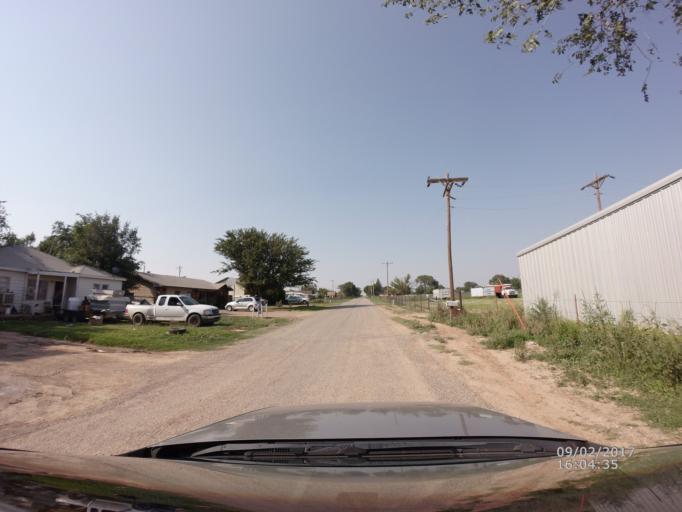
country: US
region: New Mexico
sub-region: Curry County
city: Clovis
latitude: 34.4442
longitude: -103.1996
